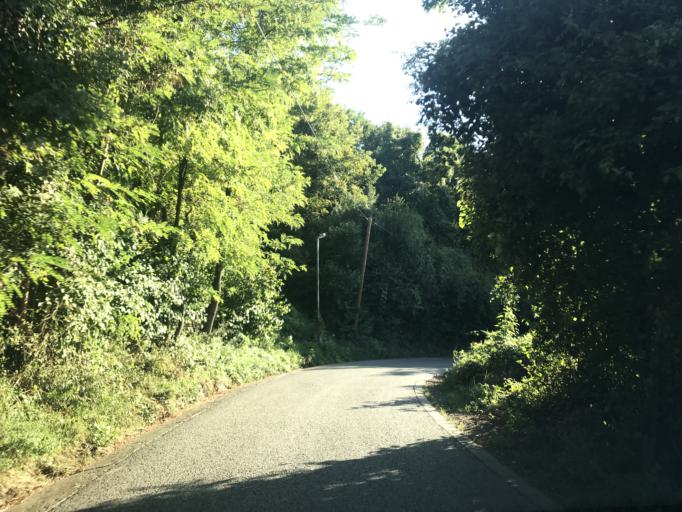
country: RS
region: Autonomna Pokrajina Vojvodina
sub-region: Juznobacki Okrug
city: Novi Sad
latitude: 45.2133
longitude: 19.8027
